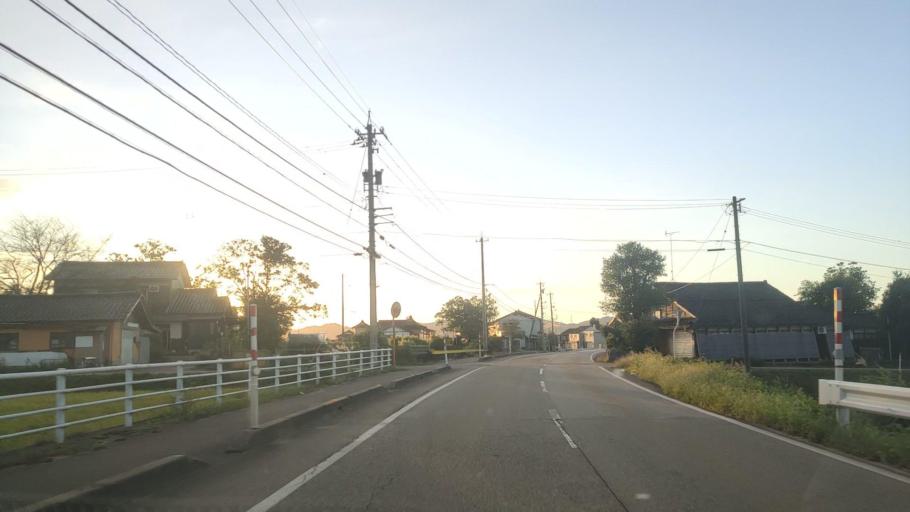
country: JP
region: Toyama
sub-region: Oyabe Shi
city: Oyabe
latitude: 36.6303
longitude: 136.8729
